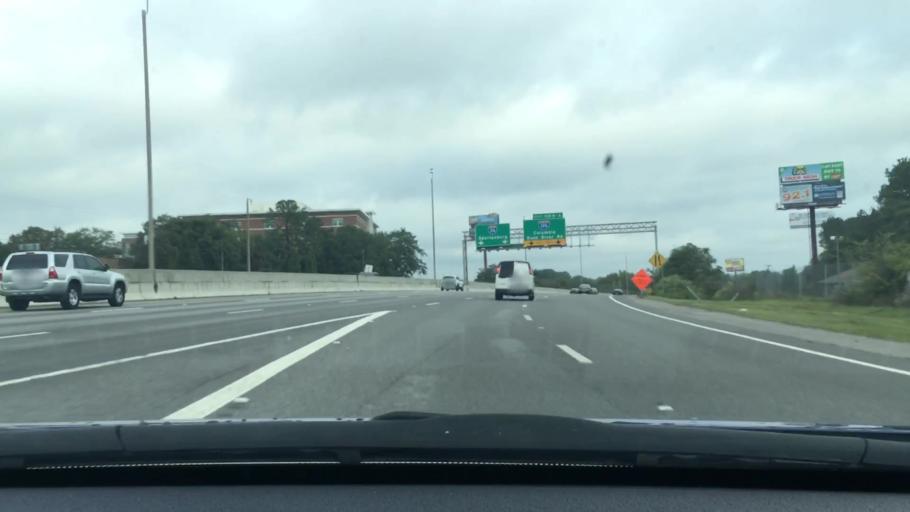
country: US
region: South Carolina
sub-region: Lexington County
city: West Columbia
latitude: 34.0057
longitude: -81.1106
